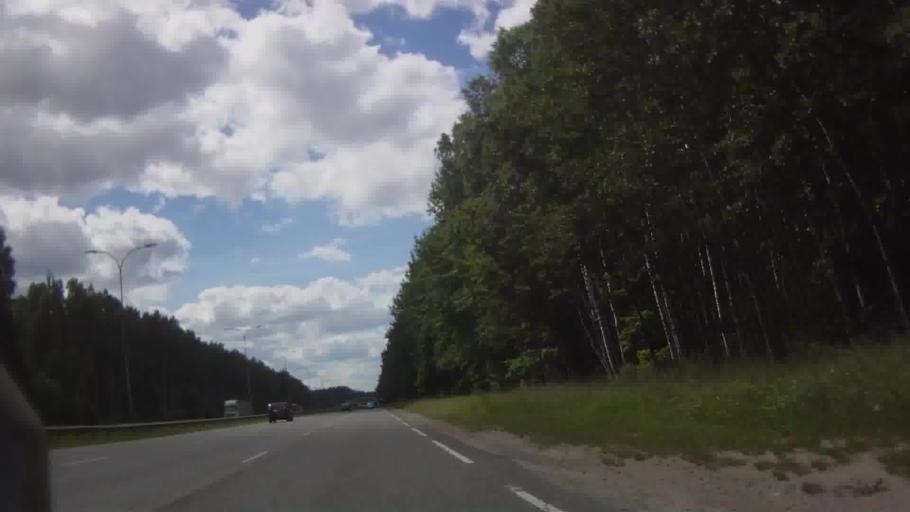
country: LV
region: Babite
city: Pinki
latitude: 56.9502
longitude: 23.9730
